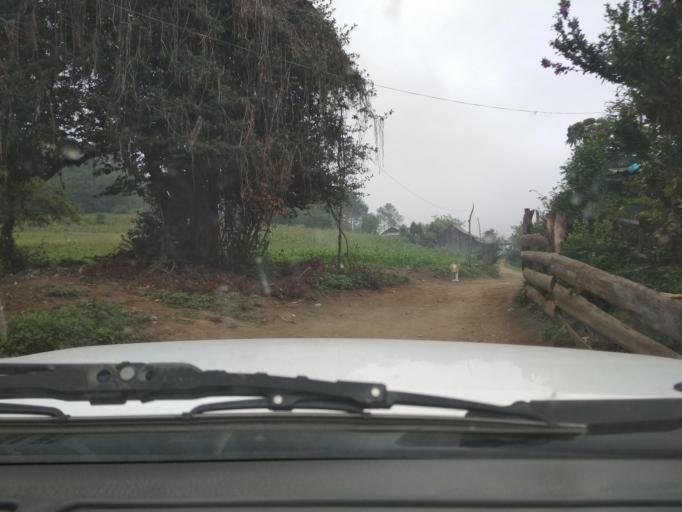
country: MX
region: Veracruz
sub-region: La Perla
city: Chilapa
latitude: 18.9965
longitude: -97.1468
